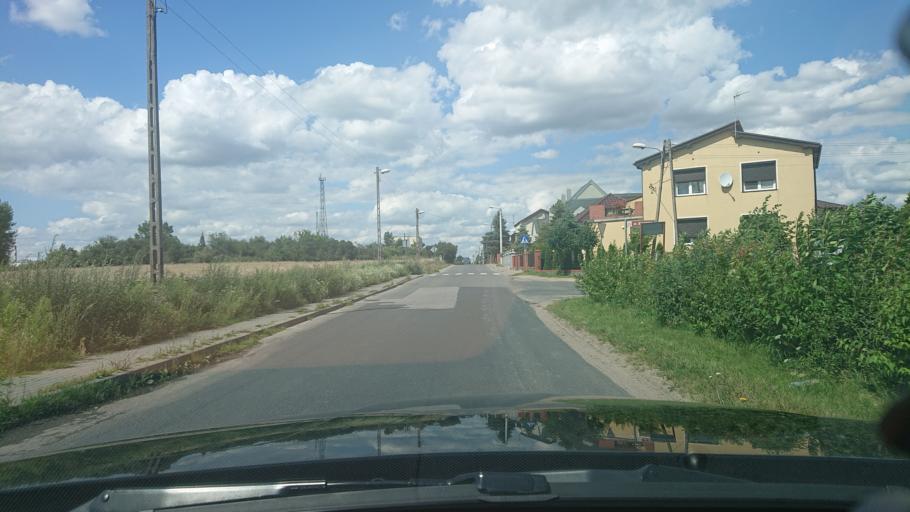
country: PL
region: Greater Poland Voivodeship
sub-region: Powiat gnieznienski
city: Gniezno
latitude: 52.5383
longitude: 17.6340
